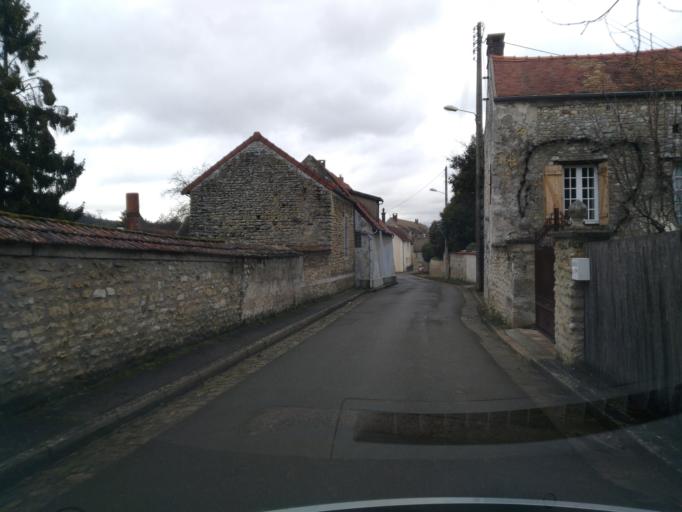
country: FR
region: Ile-de-France
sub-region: Departement des Yvelines
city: Mantes-la-Ville
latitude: 48.9536
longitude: 1.7101
